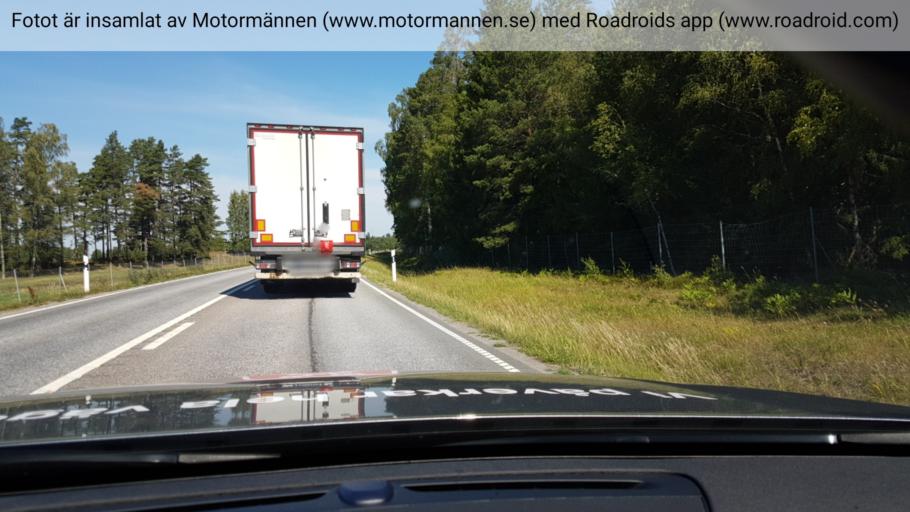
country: SE
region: OErebro
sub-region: Hallsbergs Kommun
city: Palsboda
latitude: 58.9949
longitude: 15.4057
